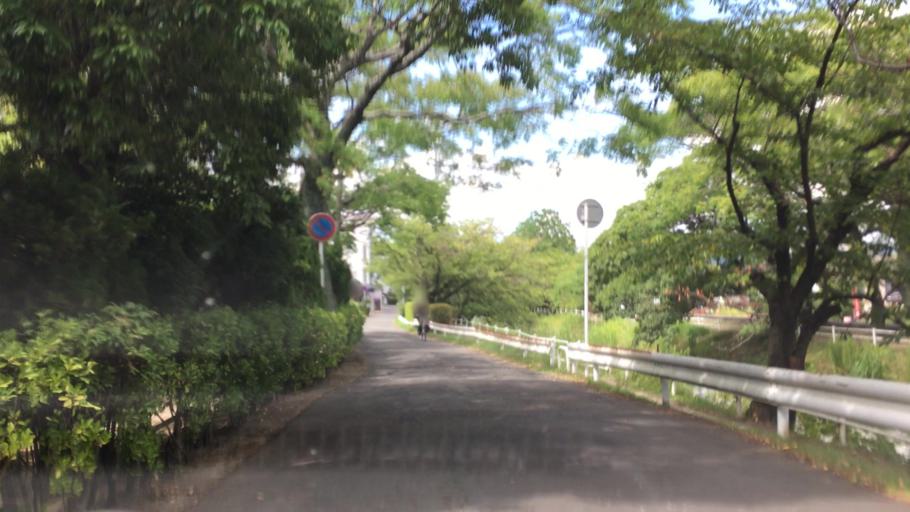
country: JP
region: Saga Prefecture
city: Saga-shi
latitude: 33.2658
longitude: 130.2829
